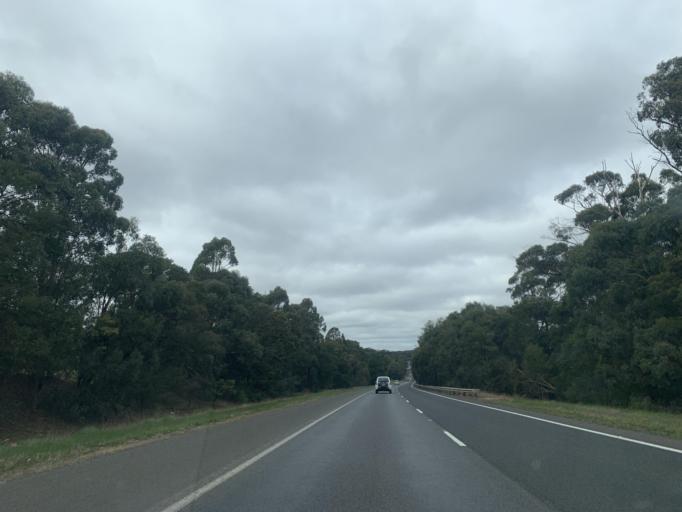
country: AU
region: Victoria
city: Brown Hill
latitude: -37.5396
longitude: 143.8852
